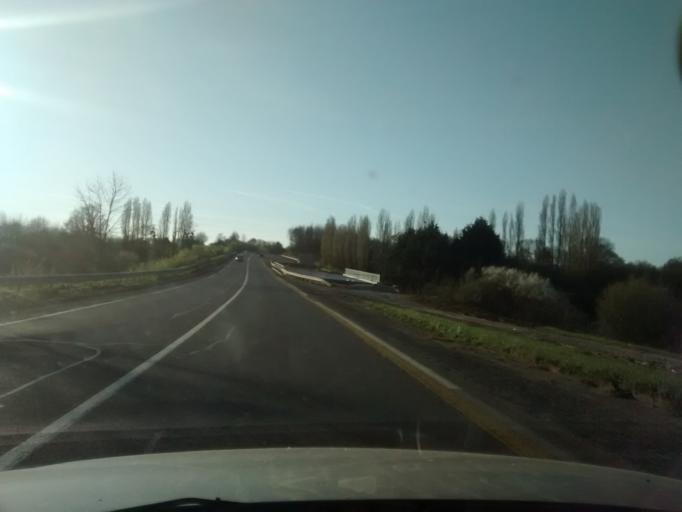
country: FR
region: Pays de la Loire
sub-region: Departement de la Sarthe
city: Sarge-les-le-Mans
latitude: 48.0266
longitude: 0.2235
